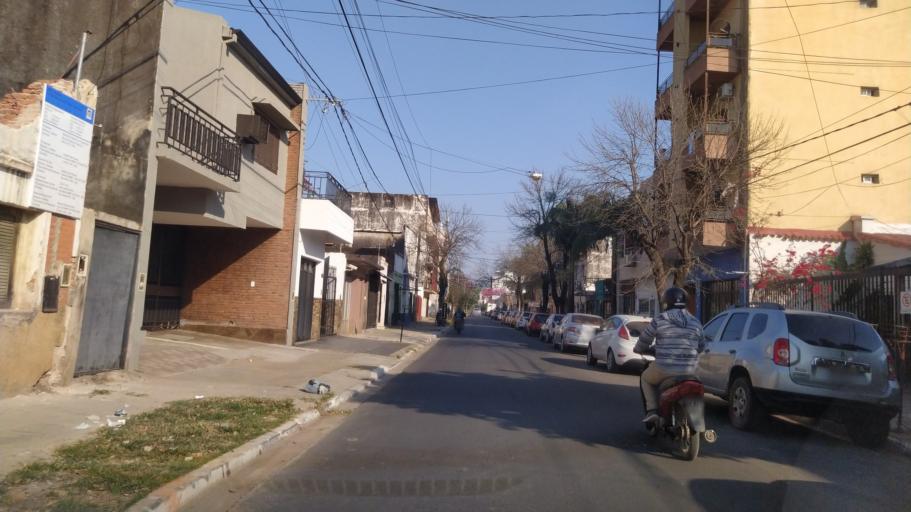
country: AR
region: Corrientes
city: Corrientes
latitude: -27.4737
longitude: -58.8211
